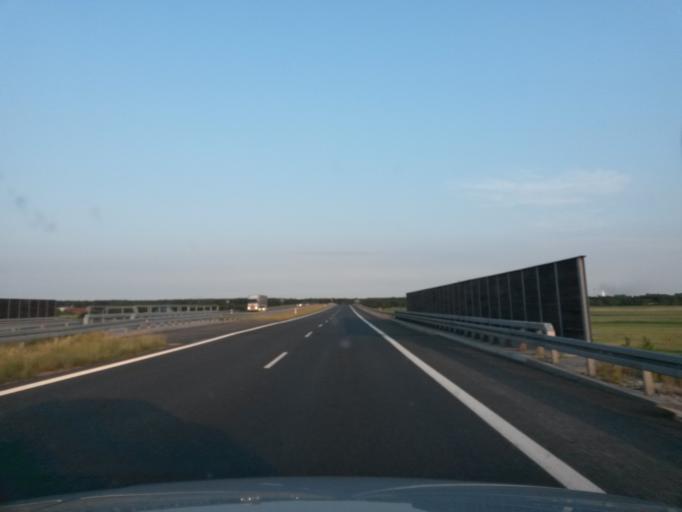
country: PL
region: Lodz Voivodeship
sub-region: Powiat wieruszowski
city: Wieruszow
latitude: 51.3209
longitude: 18.1607
